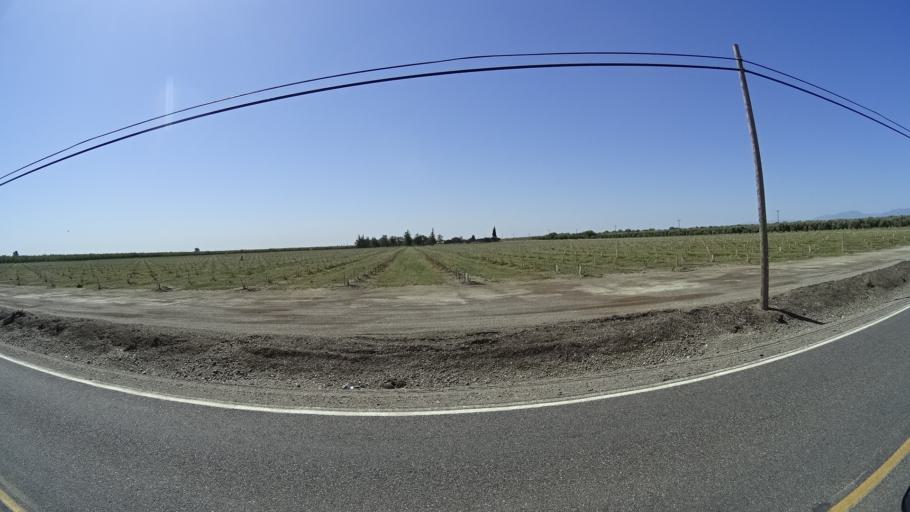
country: US
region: California
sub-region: Glenn County
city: Orland
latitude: 39.7107
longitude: -122.1391
